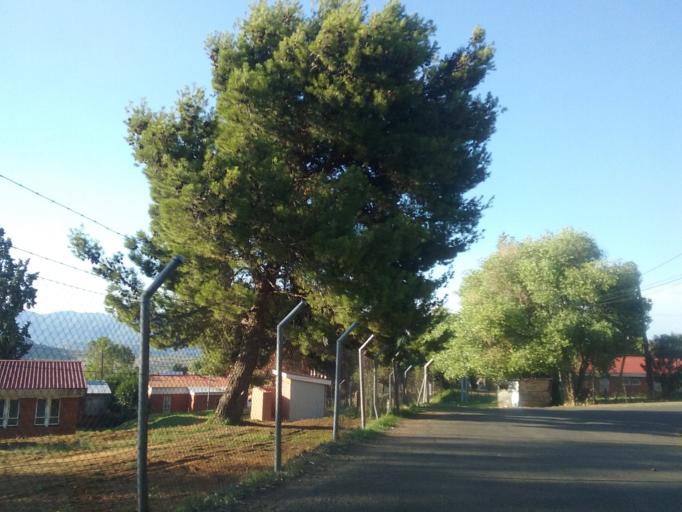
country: LS
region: Quthing
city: Quthing
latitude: -30.4055
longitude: 27.7062
